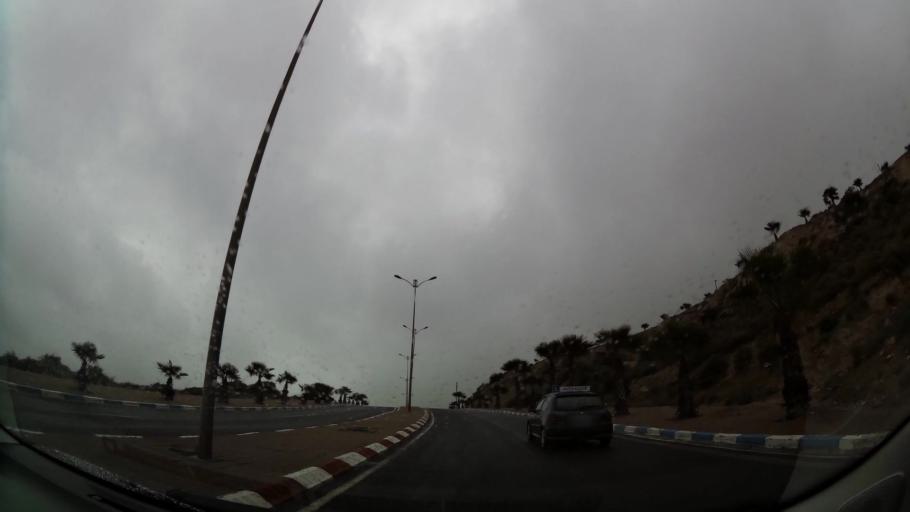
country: MA
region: Taza-Al Hoceima-Taounate
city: Tirhanimine
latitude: 35.2465
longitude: -3.9567
